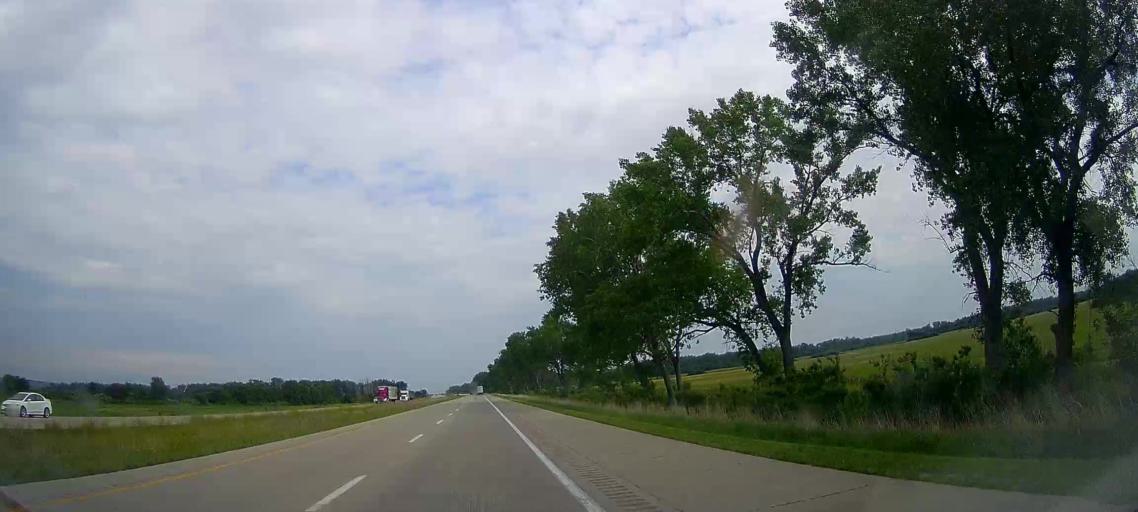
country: US
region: Nebraska
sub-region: Burt County
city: Tekamah
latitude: 41.8267
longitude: -96.0778
